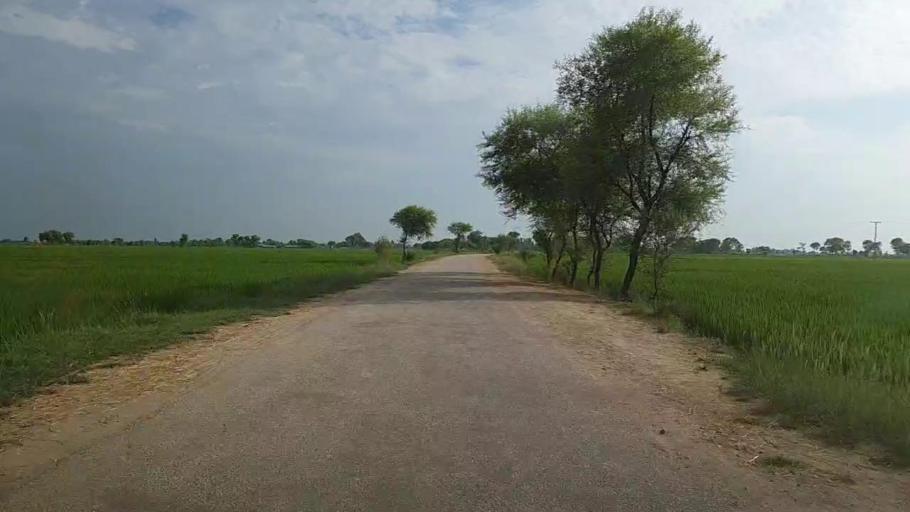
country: PK
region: Sindh
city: Thul
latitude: 28.2616
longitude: 68.8591
